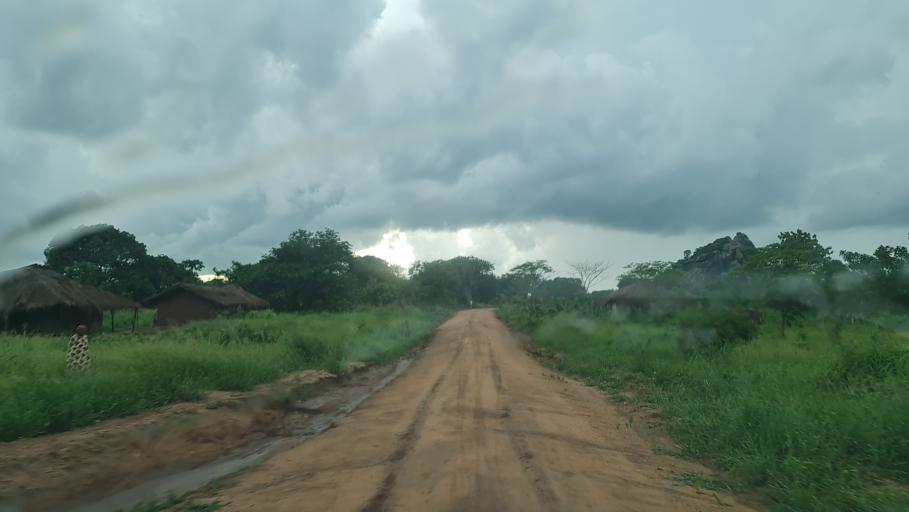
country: MZ
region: Nampula
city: Nacala
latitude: -13.9846
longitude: 40.3966
